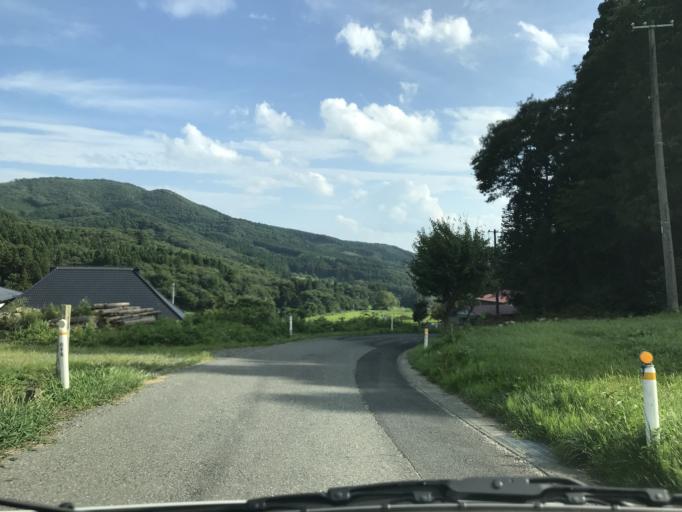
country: JP
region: Iwate
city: Ofunato
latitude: 38.9644
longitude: 141.4723
